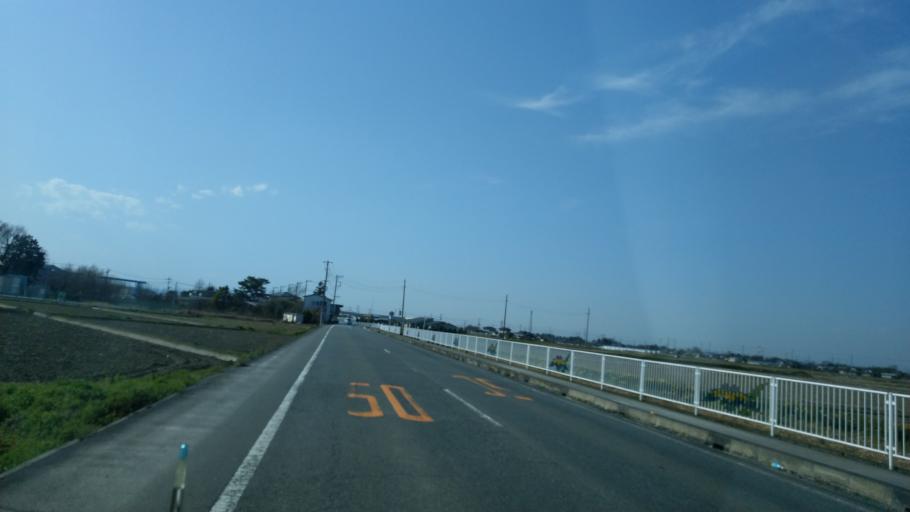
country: JP
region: Saitama
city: Kawagoe
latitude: 35.9859
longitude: 139.4742
